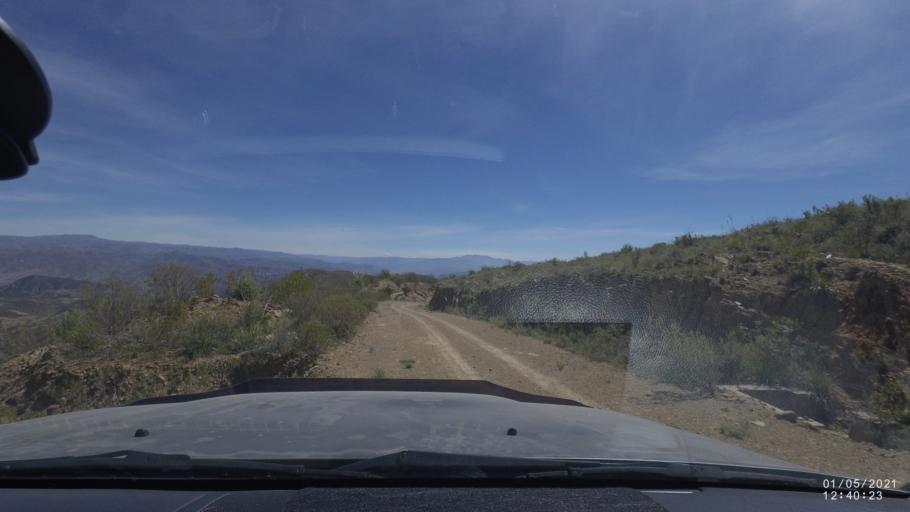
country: BO
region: Cochabamba
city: Capinota
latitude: -17.6806
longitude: -66.1592
